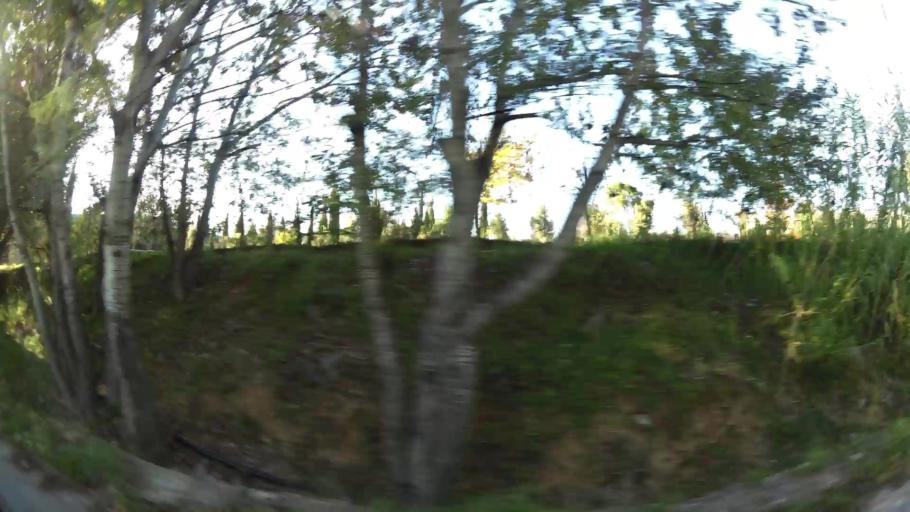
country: GR
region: Attica
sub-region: Nomarchia Anatolikis Attikis
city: Anoixi
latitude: 38.1287
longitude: 23.8471
